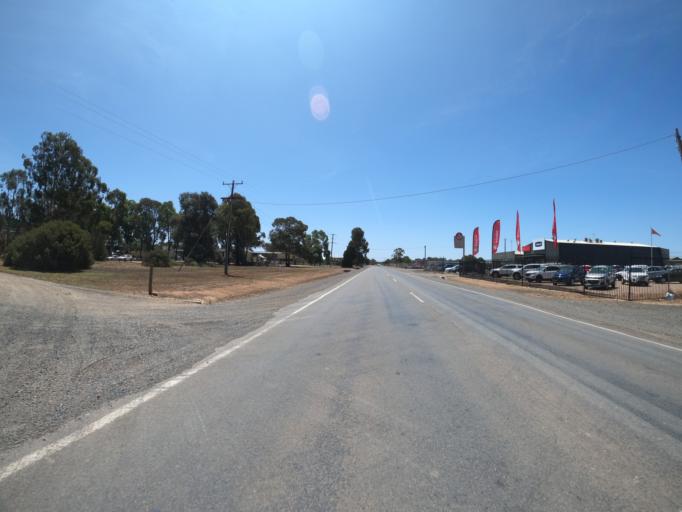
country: AU
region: Victoria
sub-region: Moira
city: Yarrawonga
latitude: -36.0315
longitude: 145.9955
